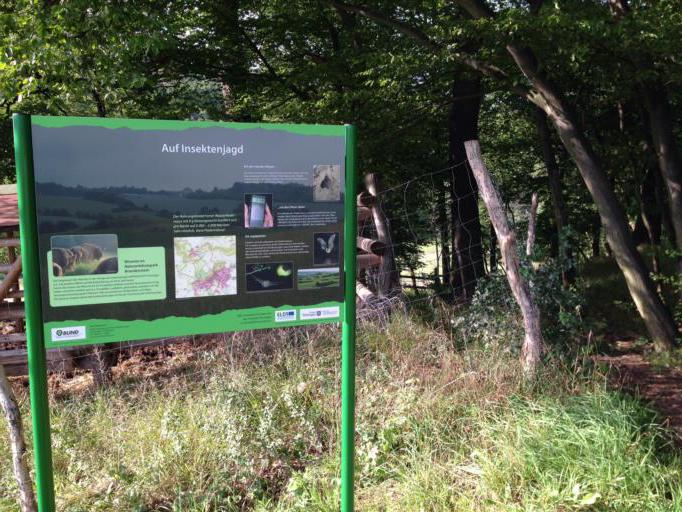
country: DE
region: Thuringia
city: Ranis
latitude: 50.6671
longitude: 11.5578
